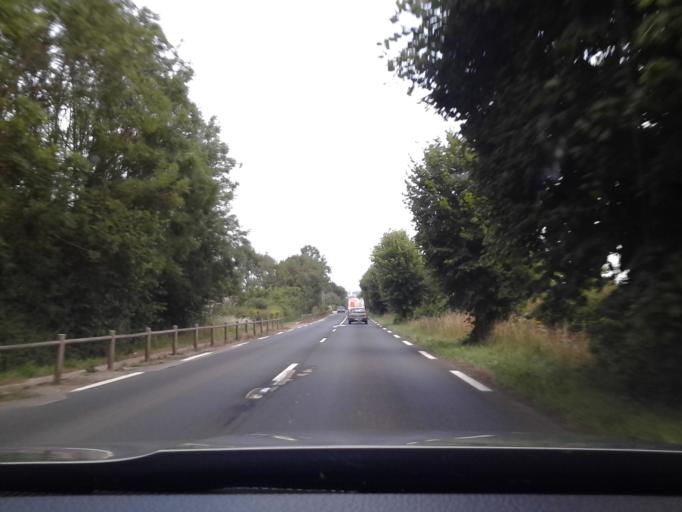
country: FR
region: Lower Normandy
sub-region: Departement de la Manche
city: Valognes
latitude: 49.5176
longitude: -1.4914
